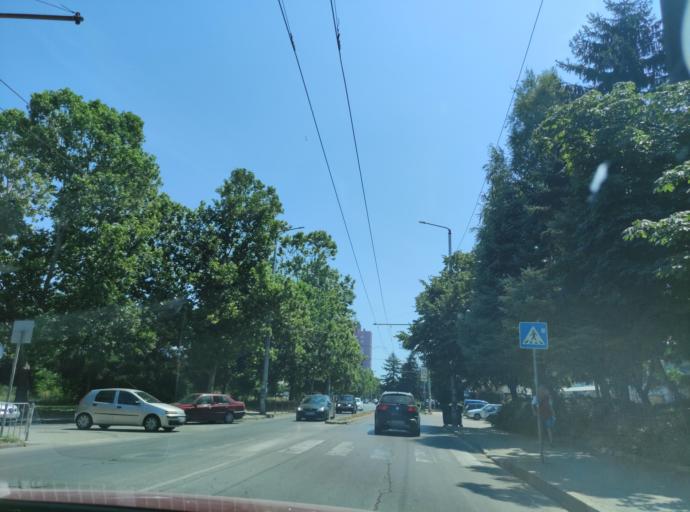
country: BG
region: Pleven
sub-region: Obshtina Pleven
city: Pleven
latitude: 43.4237
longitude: 24.5973
